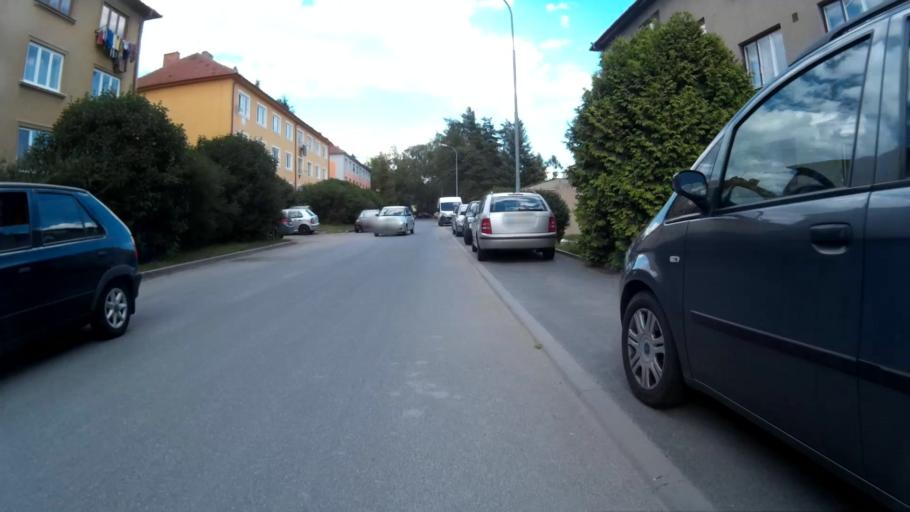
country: CZ
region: South Moravian
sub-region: Okres Brno-Venkov
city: Rosice
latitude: 49.1804
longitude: 16.3991
